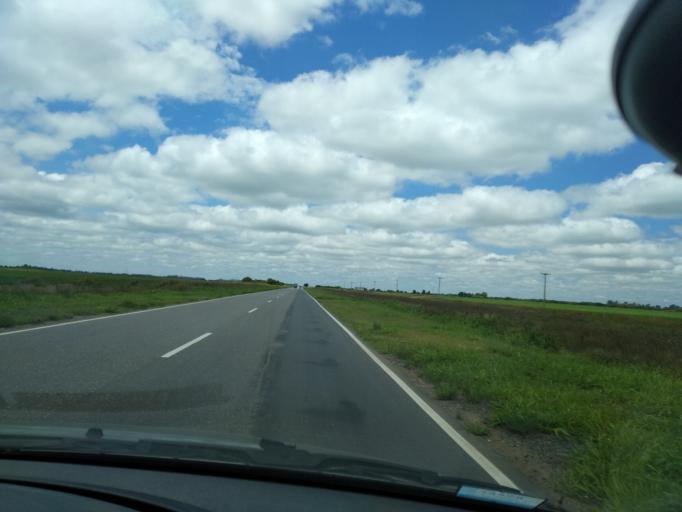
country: AR
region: Cordoba
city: Toledo
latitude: -31.6450
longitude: -64.0081
